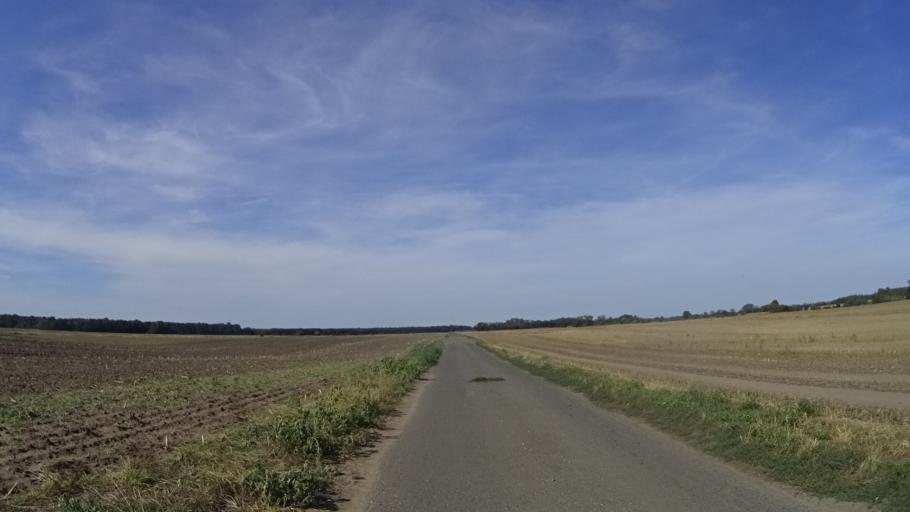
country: AT
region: Lower Austria
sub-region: Politischer Bezirk Ganserndorf
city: Durnkrut
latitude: 48.4390
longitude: 16.8750
